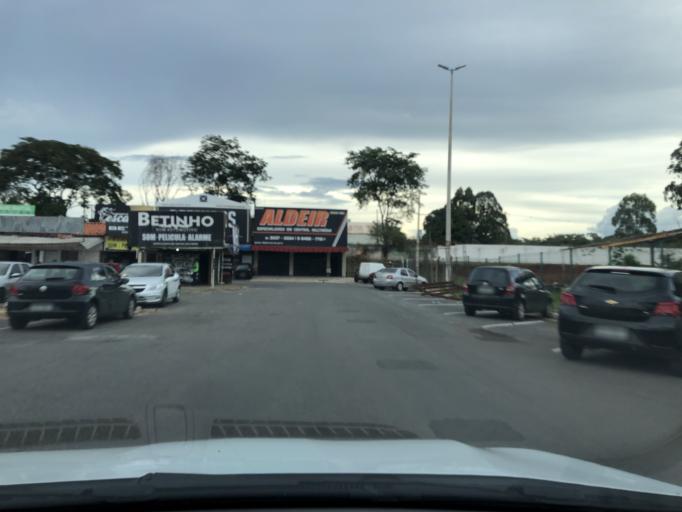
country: BR
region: Federal District
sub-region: Brasilia
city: Brasilia
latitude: -15.7950
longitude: -47.9510
